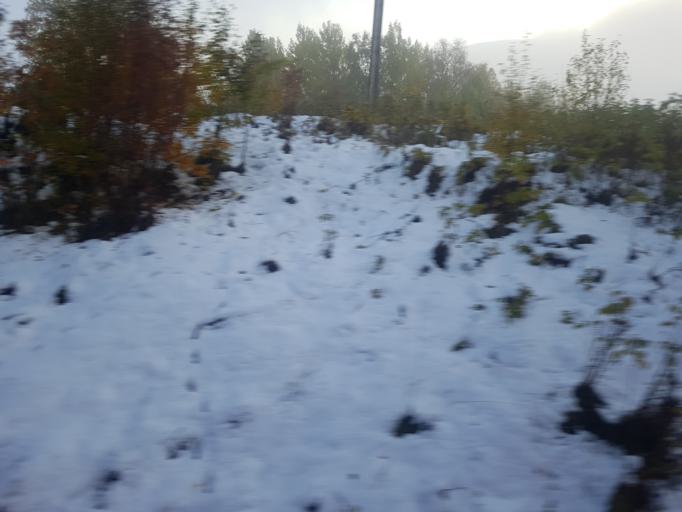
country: NO
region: Sor-Trondelag
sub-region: Oppdal
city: Oppdal
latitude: 62.5741
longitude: 9.6500
